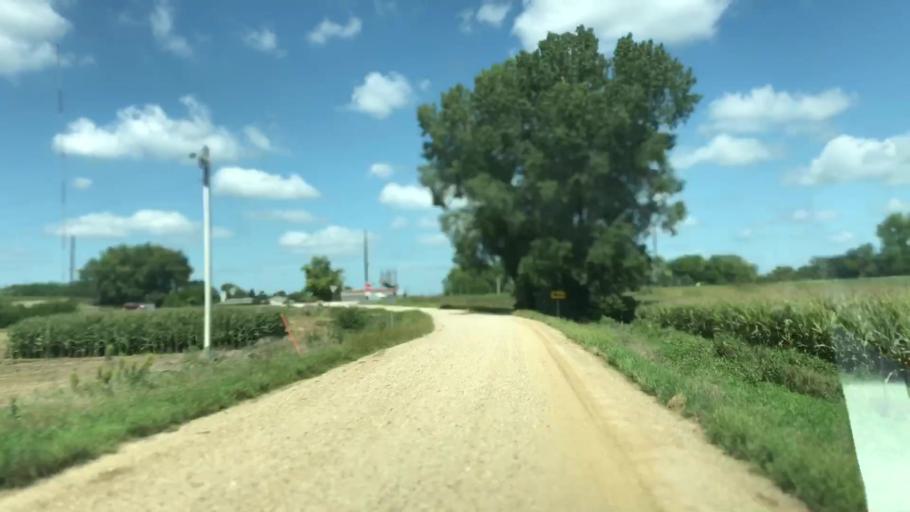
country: US
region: Iowa
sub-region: Woodbury County
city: Sergeant Bluff
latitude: 42.4737
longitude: -96.2523
